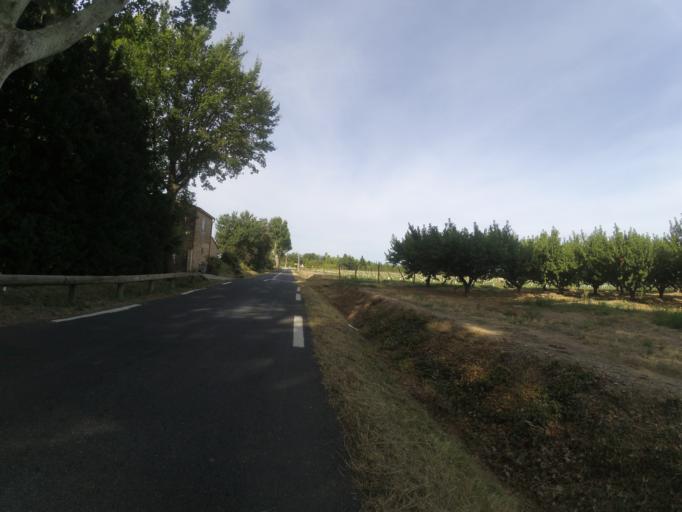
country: FR
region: Languedoc-Roussillon
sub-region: Departement des Pyrenees-Orientales
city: Millas
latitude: 42.6697
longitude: 2.7074
